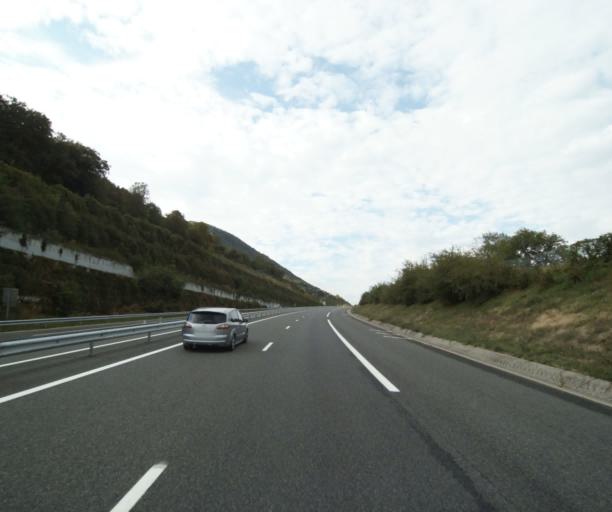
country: FR
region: Rhone-Alpes
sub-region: Departement de l'Isere
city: Vif
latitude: 45.0252
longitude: 5.6624
